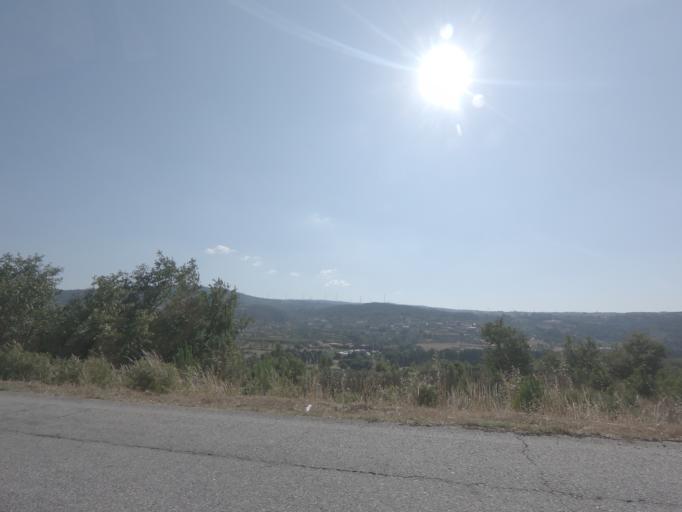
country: PT
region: Viseu
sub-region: Moimenta da Beira
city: Moimenta da Beira
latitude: 40.9785
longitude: -7.5784
